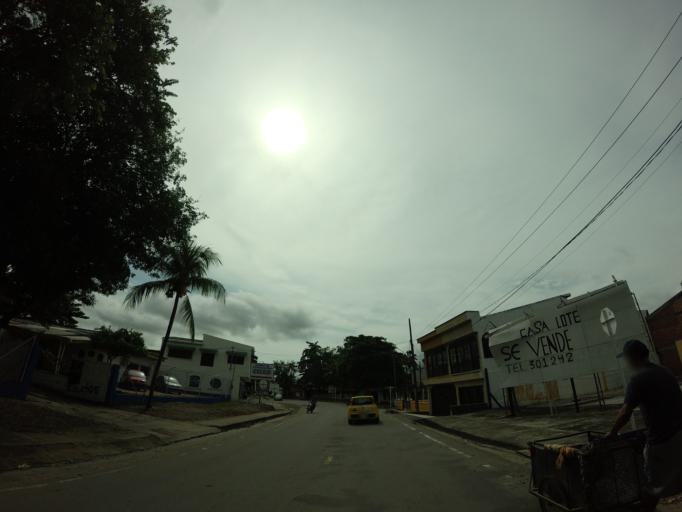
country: CO
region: Caldas
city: La Dorada
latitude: 5.4466
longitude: -74.6703
